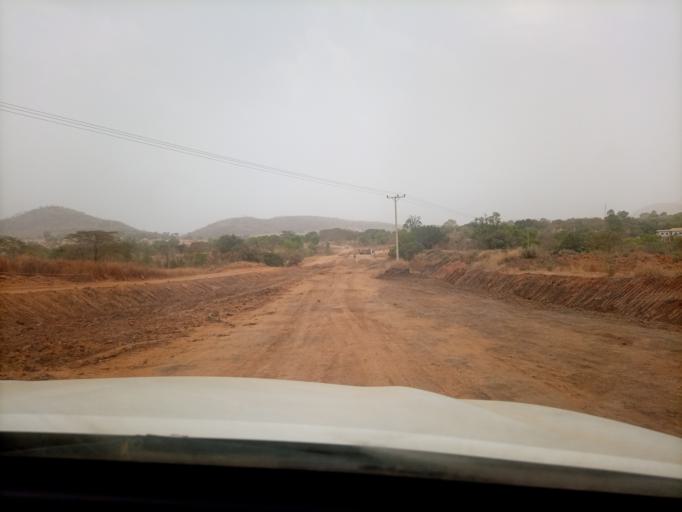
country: ET
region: Oromiya
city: Mendi
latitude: 10.2044
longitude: 35.0888
